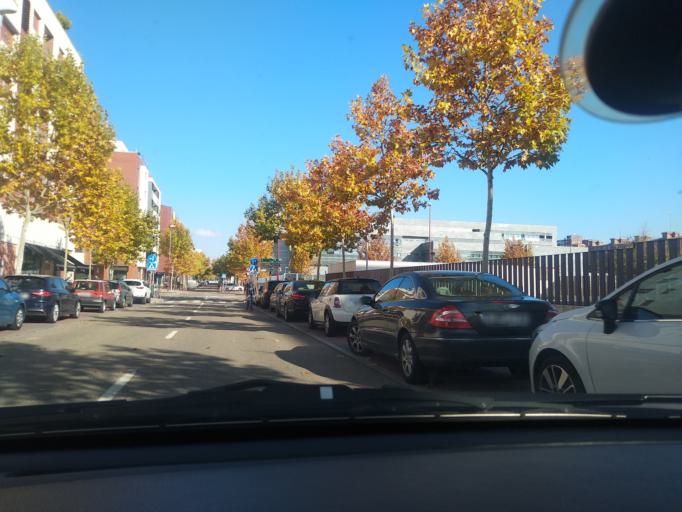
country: ES
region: Castille and Leon
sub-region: Provincia de Valladolid
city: Valladolid
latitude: 41.6445
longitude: -4.7450
